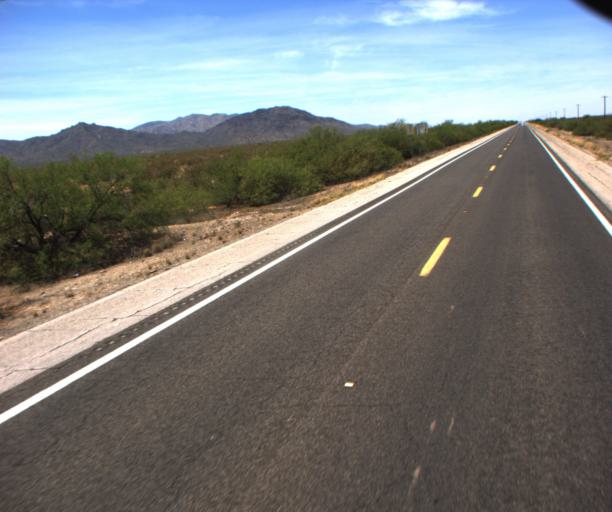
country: US
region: Arizona
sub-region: Yavapai County
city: Congress
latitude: 33.9326
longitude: -113.2126
